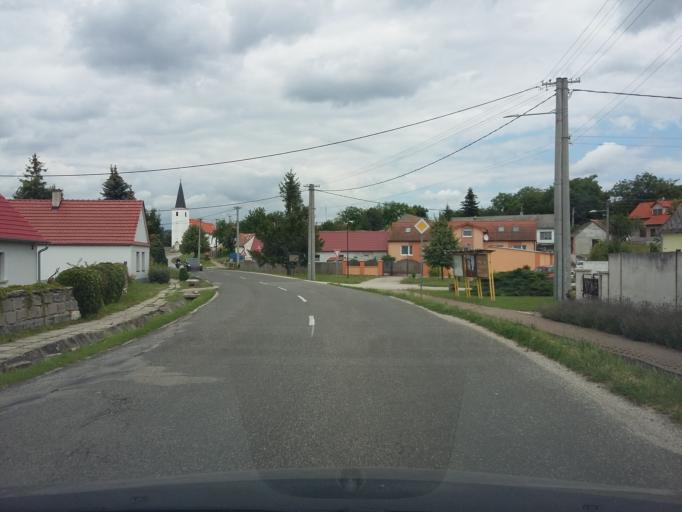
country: SK
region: Trnavsky
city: Smolenice
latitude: 48.5343
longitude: 17.3233
